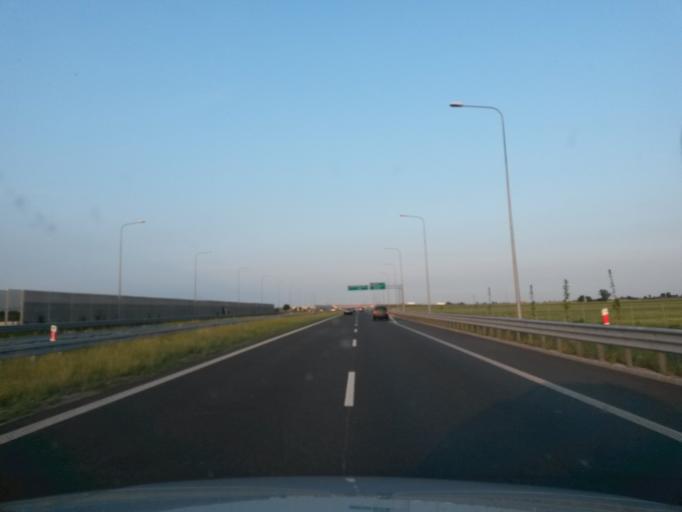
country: PL
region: Lodz Voivodeship
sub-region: Powiat wieruszowski
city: Walichnowy
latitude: 51.3175
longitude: 18.3687
